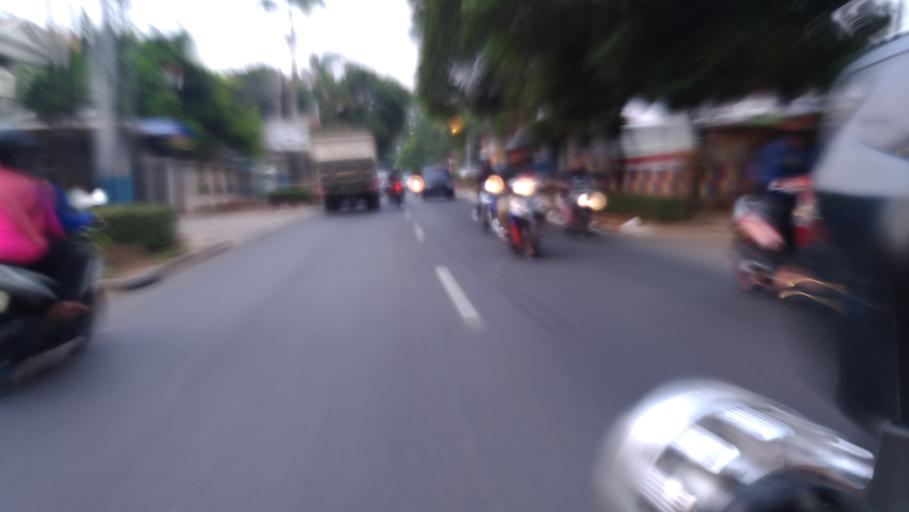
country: ID
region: West Java
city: Cileungsir
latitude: -6.3581
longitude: 106.8897
